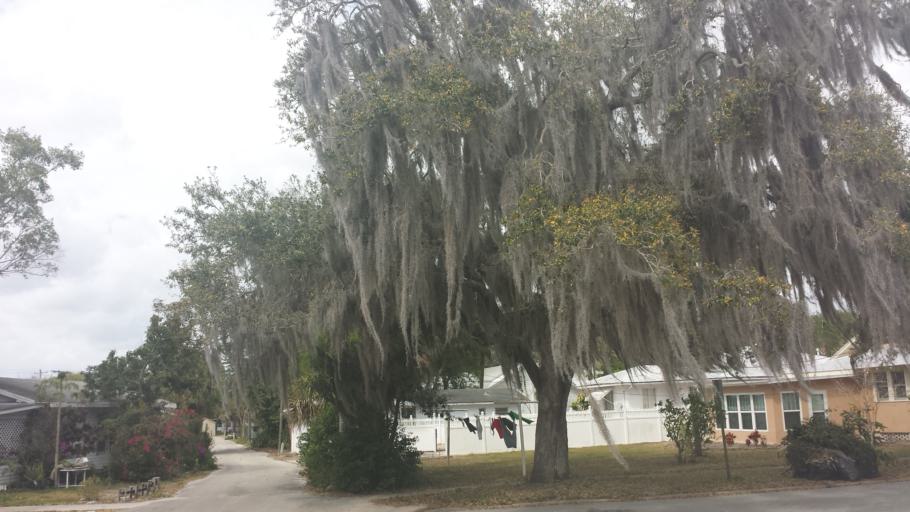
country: US
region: Florida
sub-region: Highlands County
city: Sebring
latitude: 27.4963
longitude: -81.4428
